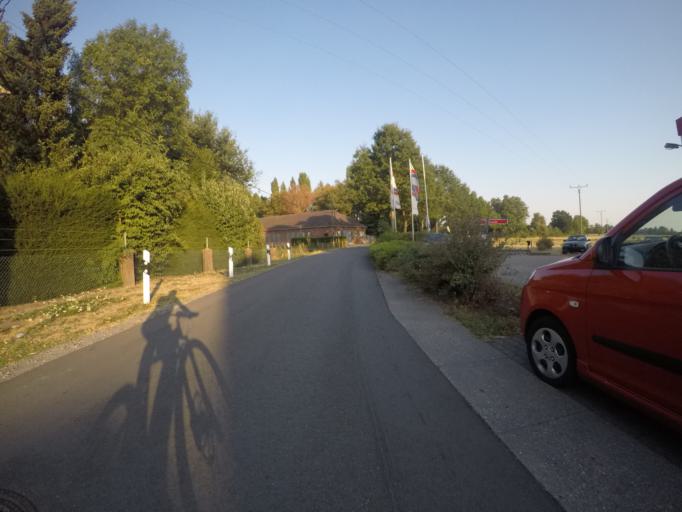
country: DE
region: North Rhine-Westphalia
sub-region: Regierungsbezirk Munster
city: Isselburg
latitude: 51.8601
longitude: 6.5124
